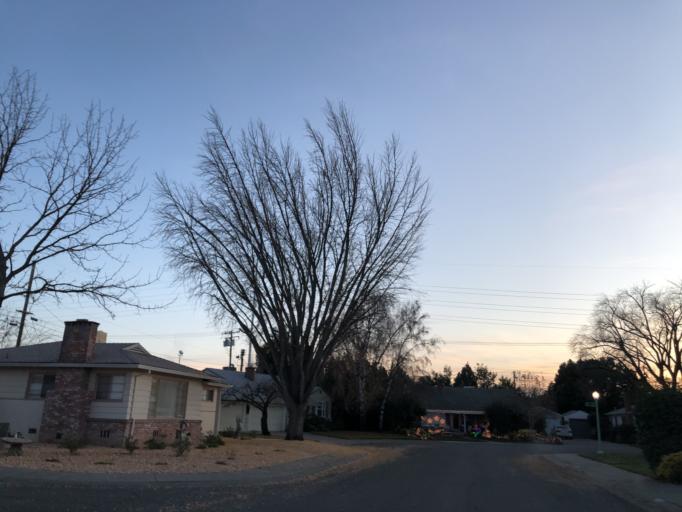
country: US
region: California
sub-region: Sacramento County
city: Sacramento
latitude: 38.5570
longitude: -121.4401
